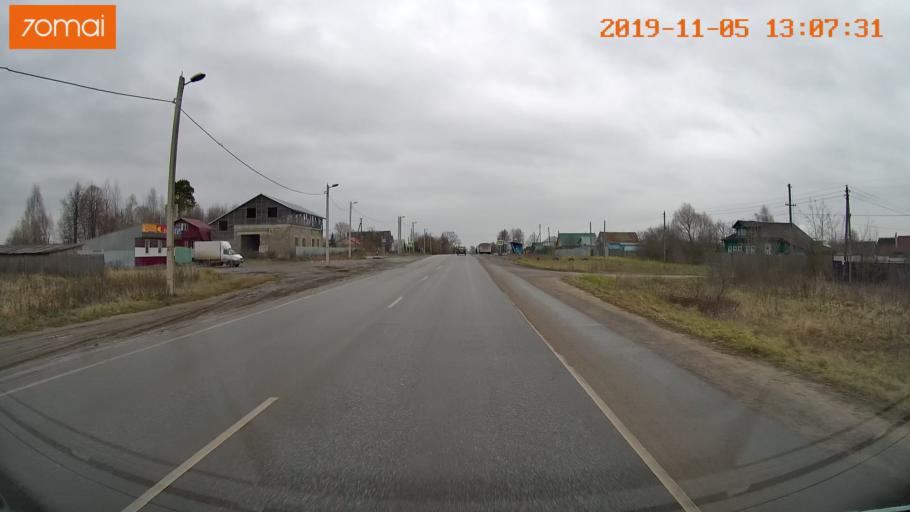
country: RU
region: Ivanovo
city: Kitovo
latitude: 56.8675
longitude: 41.2815
